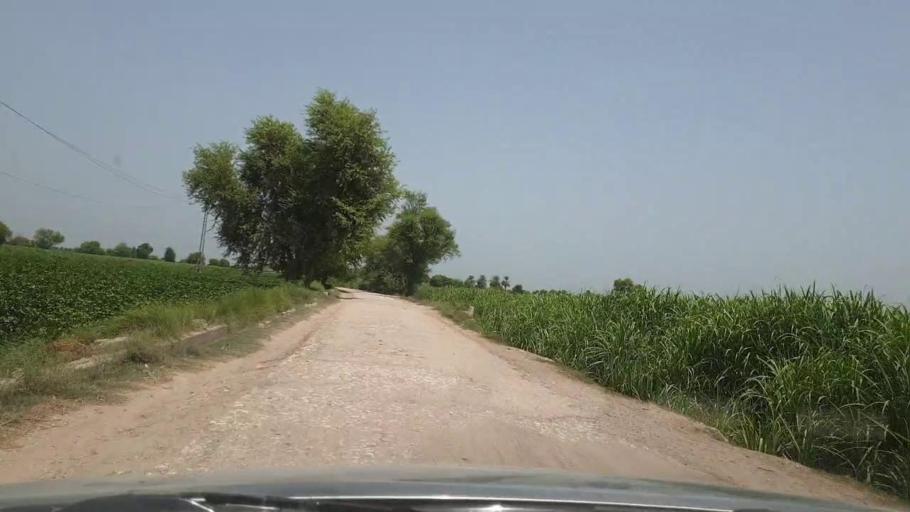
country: PK
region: Sindh
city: Pano Aqil
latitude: 27.8318
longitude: 69.1862
